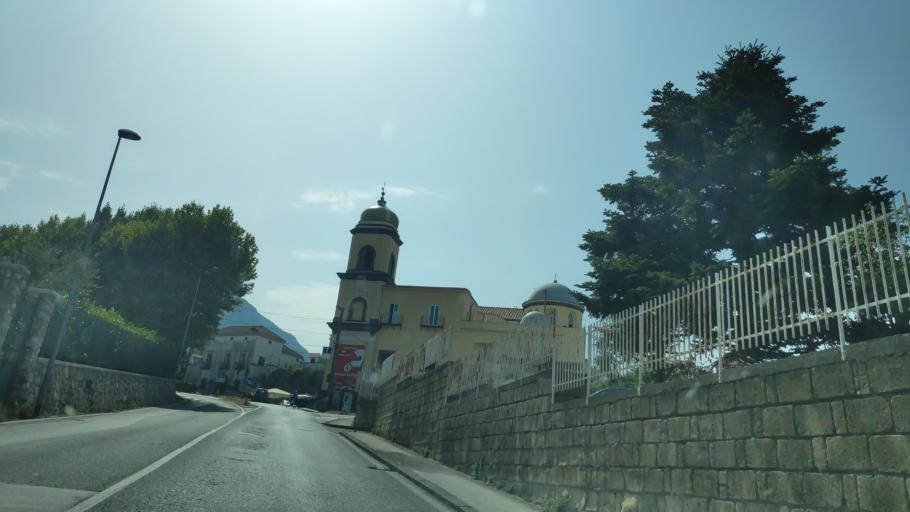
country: IT
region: Campania
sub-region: Provincia di Napoli
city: Piano di Sorrento
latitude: 40.6291
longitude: 14.4106
